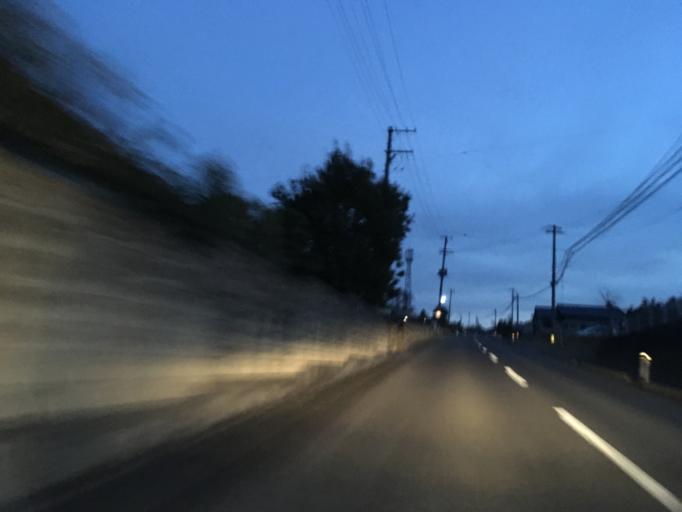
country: JP
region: Miyagi
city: Wakuya
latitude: 38.6961
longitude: 141.1634
